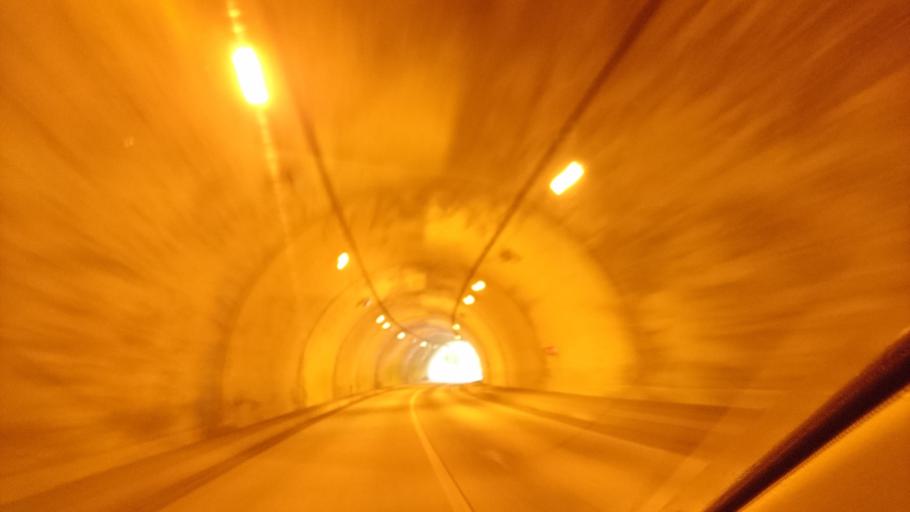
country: JP
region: Iwate
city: Mizusawa
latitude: 39.1240
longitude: 140.9074
